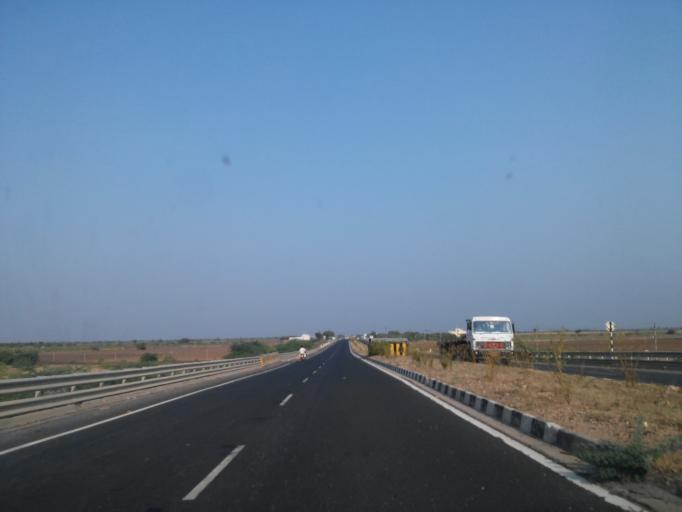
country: IN
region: Gujarat
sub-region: Surendranagar
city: Dhrangadhra
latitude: 23.0277
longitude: 71.6484
